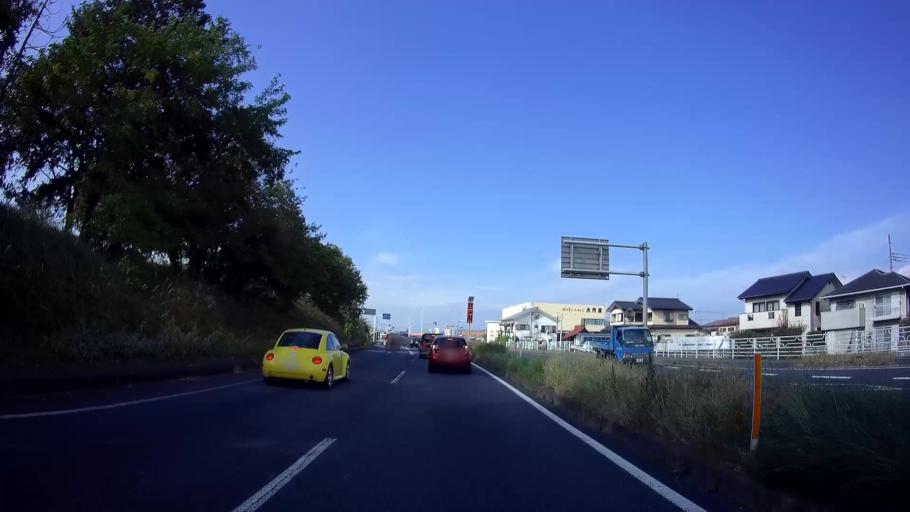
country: JP
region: Gunma
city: Takasaki
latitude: 36.3331
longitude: 138.9581
